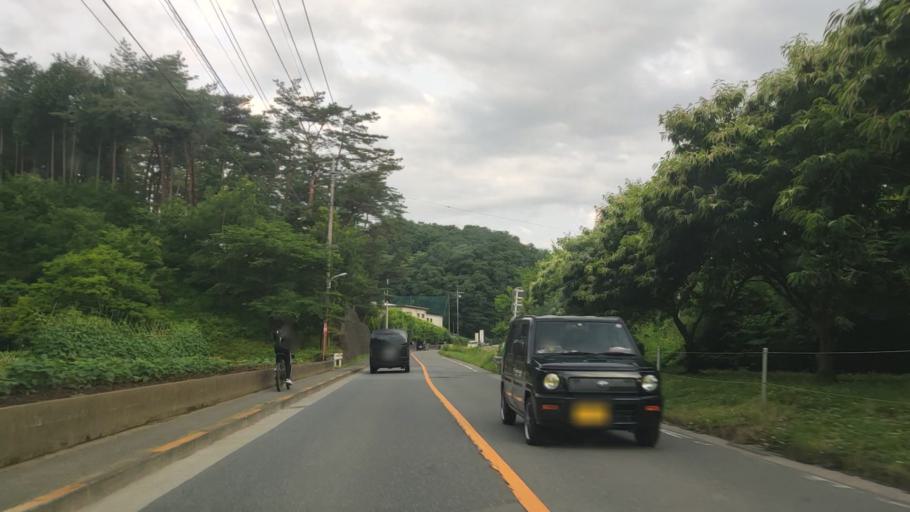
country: JP
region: Saitama
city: Hanno
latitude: 35.8170
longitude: 139.2967
